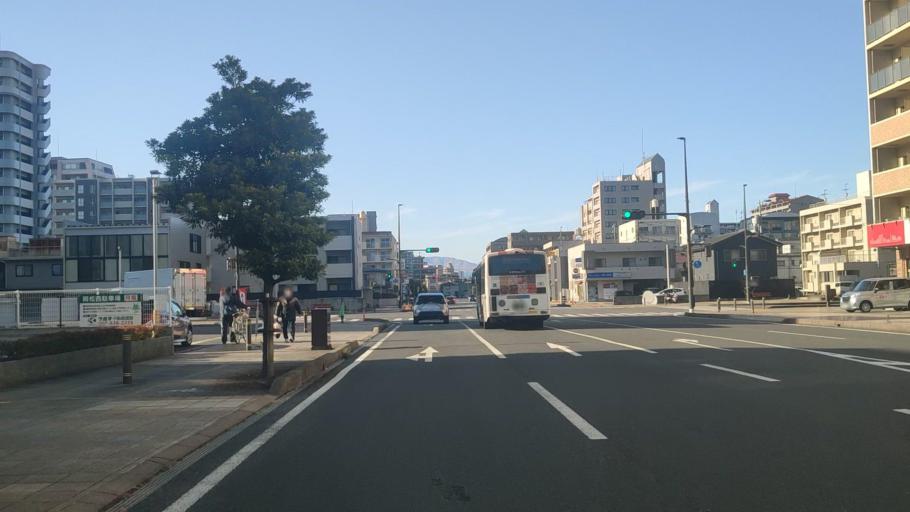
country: JP
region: Oita
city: Oita
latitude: 33.2325
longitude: 131.6039
